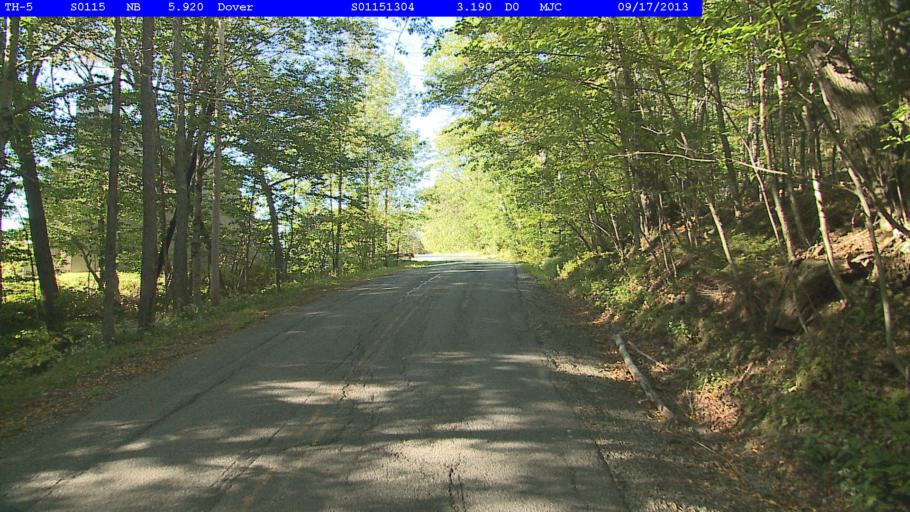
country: US
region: Vermont
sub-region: Windham County
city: Dover
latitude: 42.9700
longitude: -72.8901
